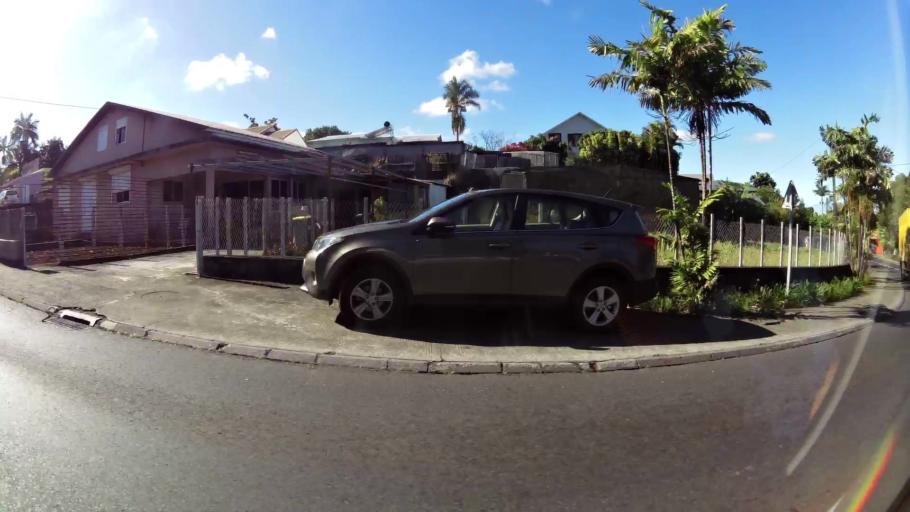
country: RE
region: Reunion
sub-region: Reunion
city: Le Tampon
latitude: -21.2695
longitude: 55.5233
